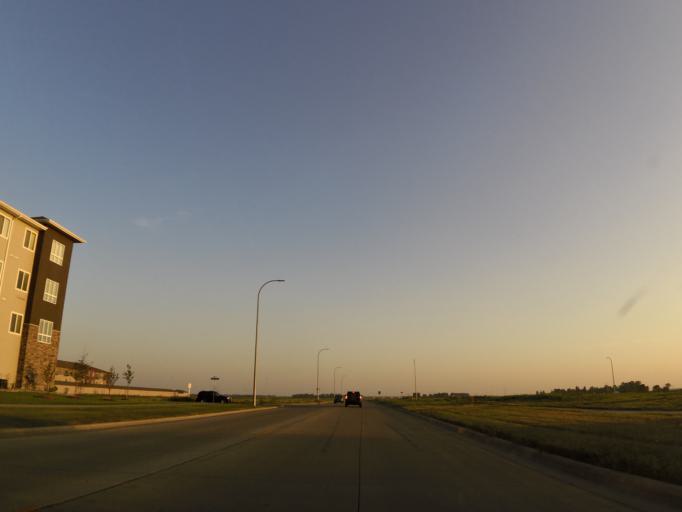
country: US
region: North Dakota
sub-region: Grand Forks County
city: Grand Forks
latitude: 47.8849
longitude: -97.0823
